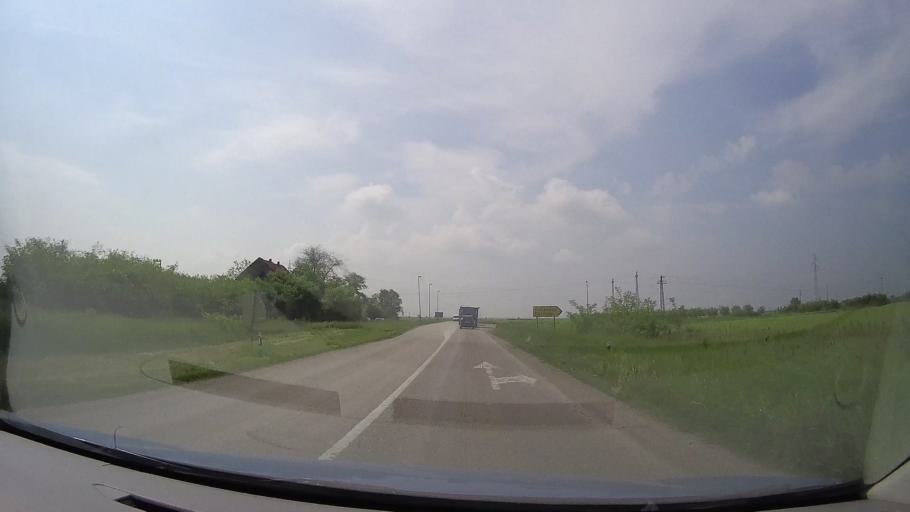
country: RS
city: Debeljaca
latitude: 45.0713
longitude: 20.6406
